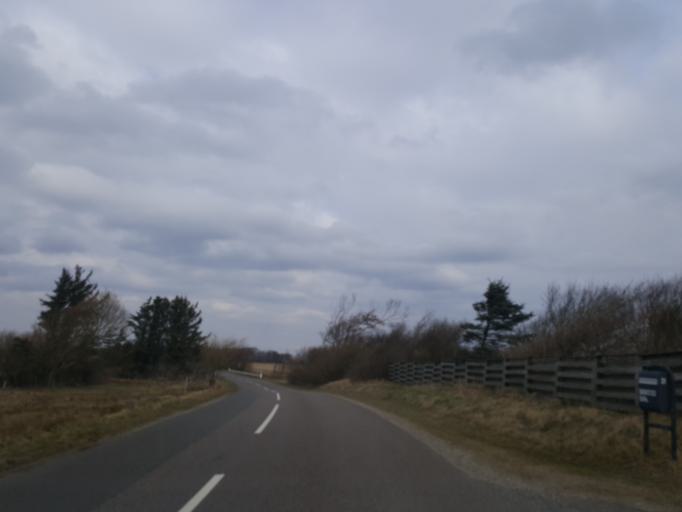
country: DK
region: Central Jutland
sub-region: Holstebro Kommune
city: Ulfborg
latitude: 56.3977
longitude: 8.2327
